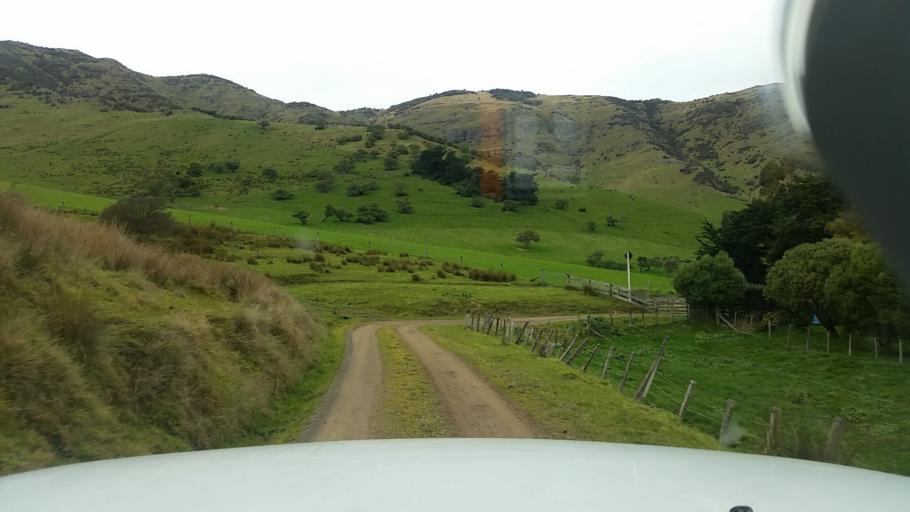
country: NZ
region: Canterbury
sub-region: Christchurch City
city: Christchurch
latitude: -43.6466
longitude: 172.8410
